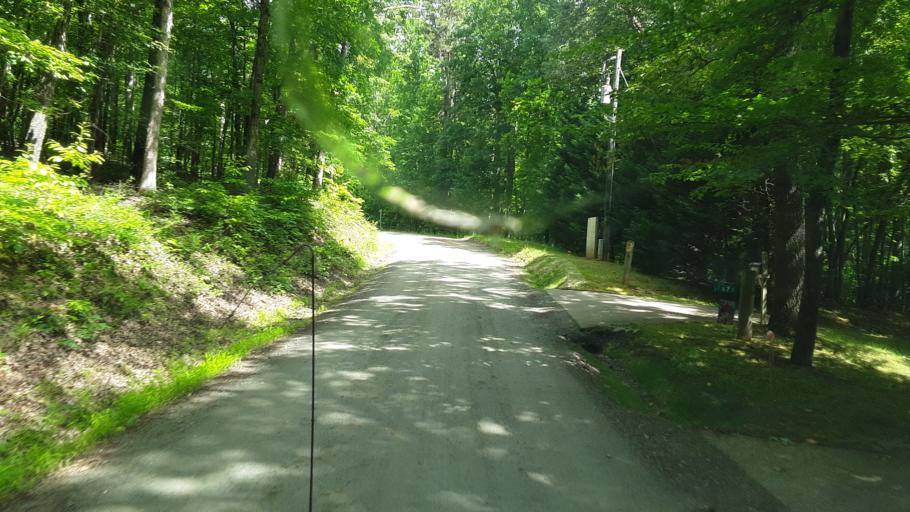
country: US
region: Virginia
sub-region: Pittsylvania County
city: Chatham
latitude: 36.8516
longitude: -79.4331
